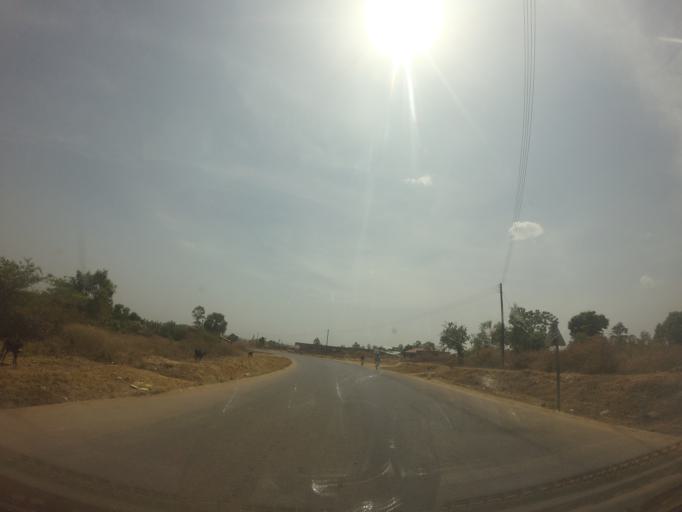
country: UG
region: Northern Region
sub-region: Arua District
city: Arua
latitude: 2.9547
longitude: 30.9175
